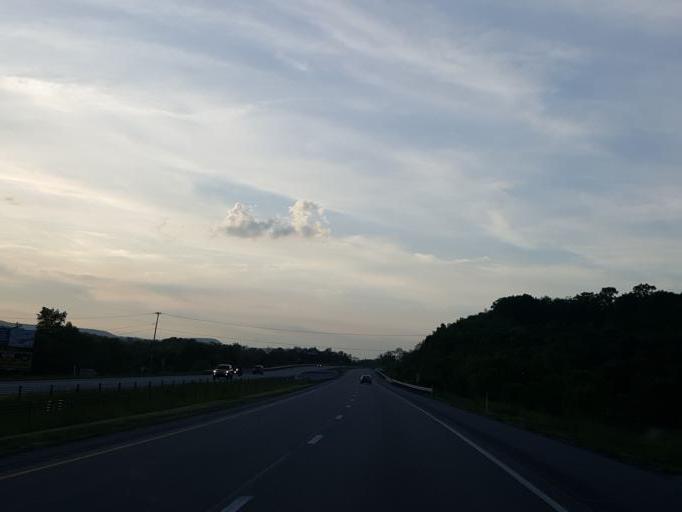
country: US
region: Pennsylvania
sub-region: Blair County
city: Duncansville
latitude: 40.3922
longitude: -78.4296
